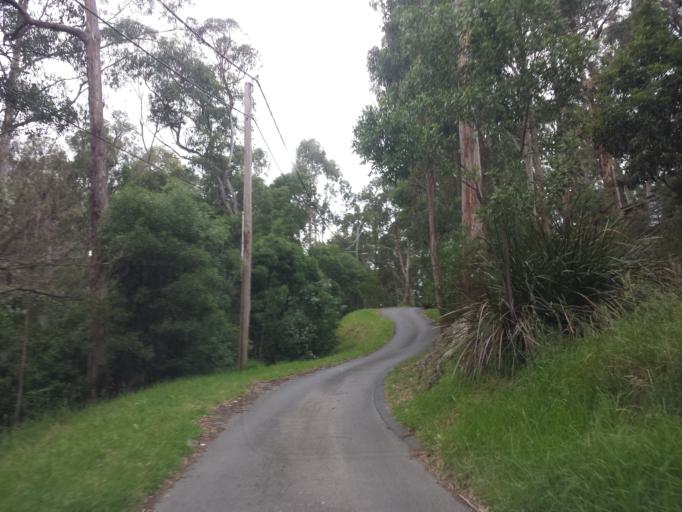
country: AU
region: Victoria
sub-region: Yarra Ranges
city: Belgrave Heights
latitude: -37.9192
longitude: 145.3380
